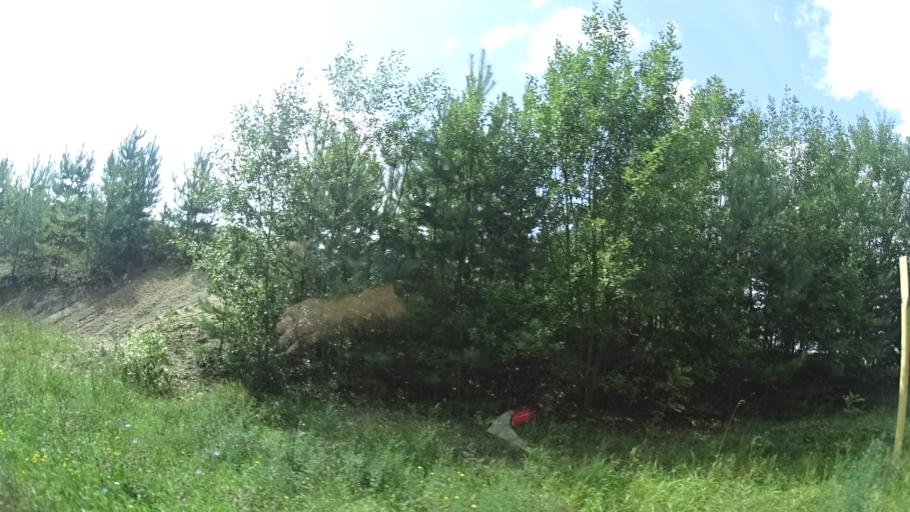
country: DE
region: Bavaria
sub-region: Upper Franconia
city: Neustadt bei Coburg
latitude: 50.2861
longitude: 11.0936
